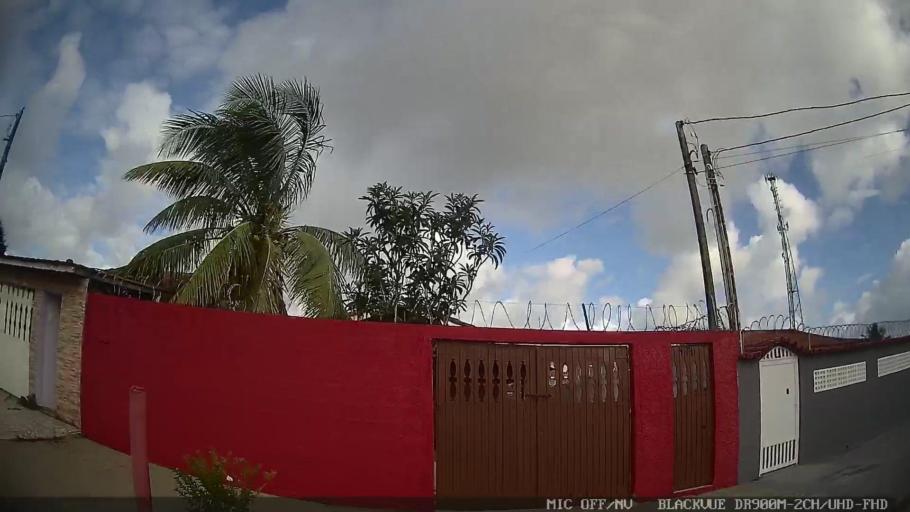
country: BR
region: Sao Paulo
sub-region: Itanhaem
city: Itanhaem
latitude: -24.1923
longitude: -46.8158
